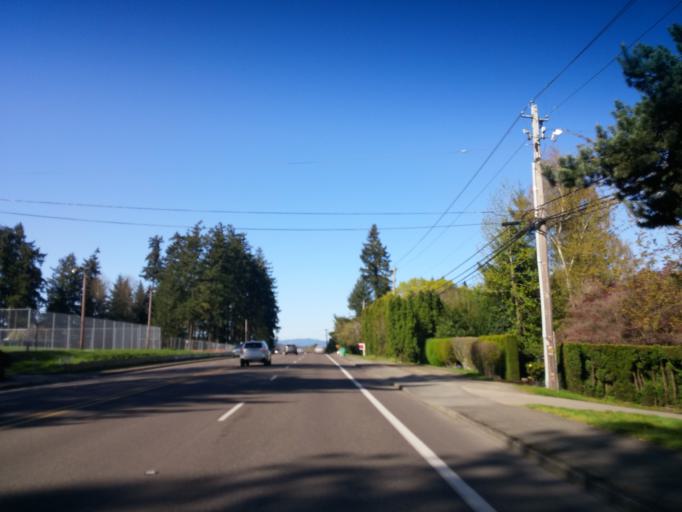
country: US
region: Oregon
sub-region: Washington County
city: Cedar Hills
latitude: 45.5036
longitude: -122.8019
